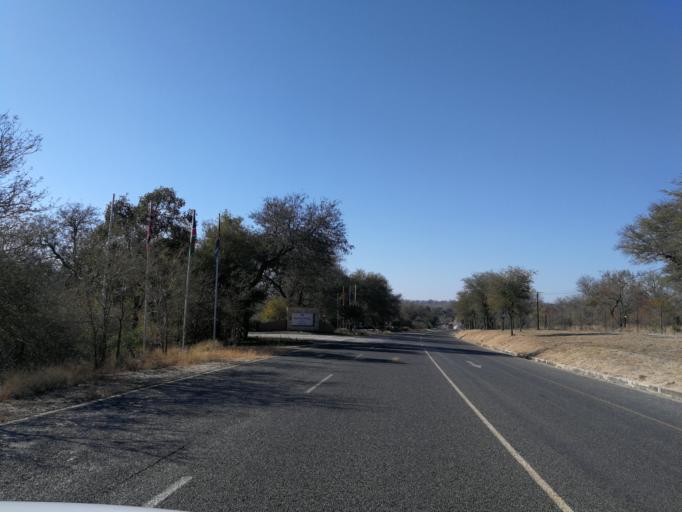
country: ZA
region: Limpopo
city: Thulamahashi
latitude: -24.9774
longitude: 31.4790
